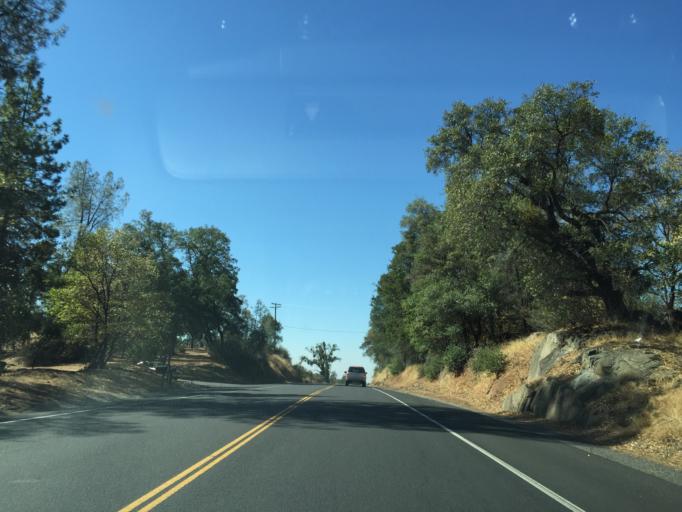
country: US
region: California
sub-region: Tuolumne County
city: Mono Vista
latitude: 37.9902
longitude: -120.2798
